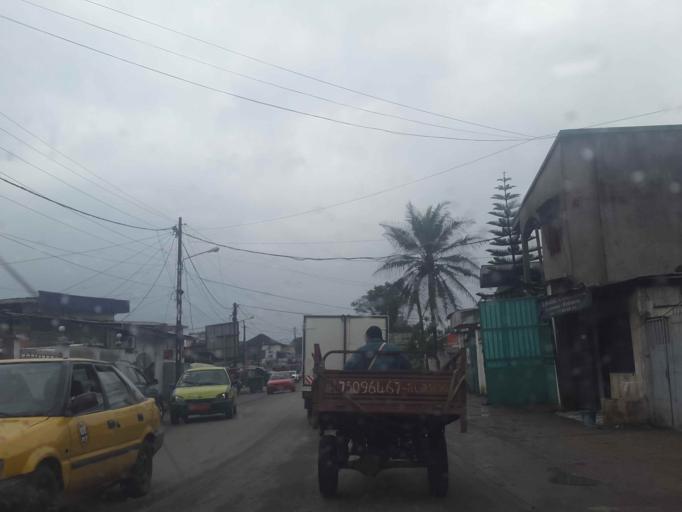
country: CM
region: Littoral
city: Douala
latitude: 4.0693
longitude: 9.7125
